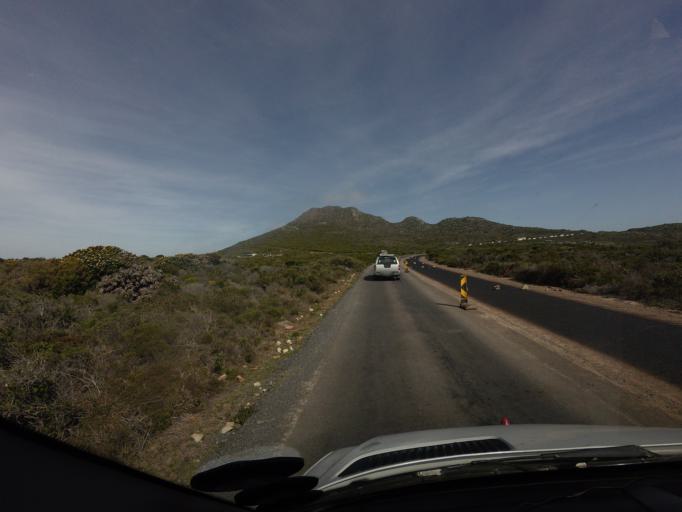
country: ZA
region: Western Cape
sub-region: City of Cape Town
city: Retreat
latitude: -34.3411
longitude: 18.4672
